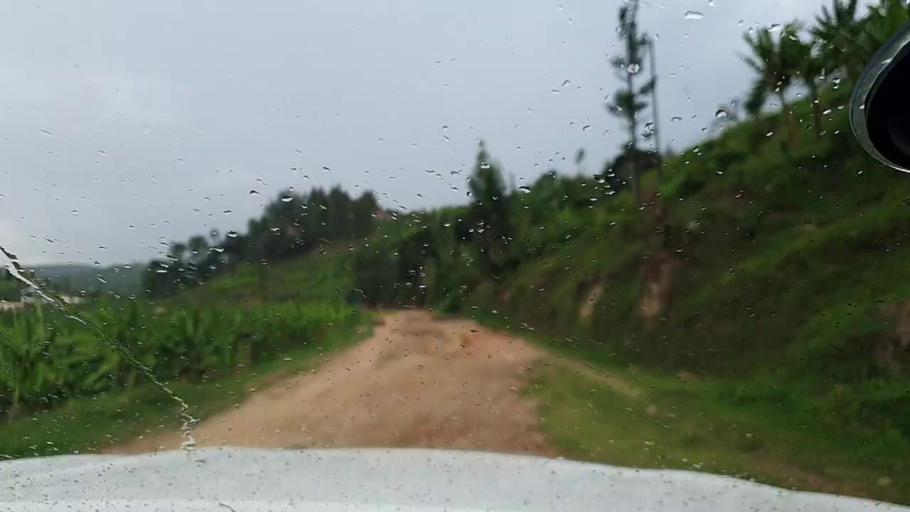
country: RW
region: Western Province
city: Kibuye
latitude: -2.0753
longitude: 29.4387
